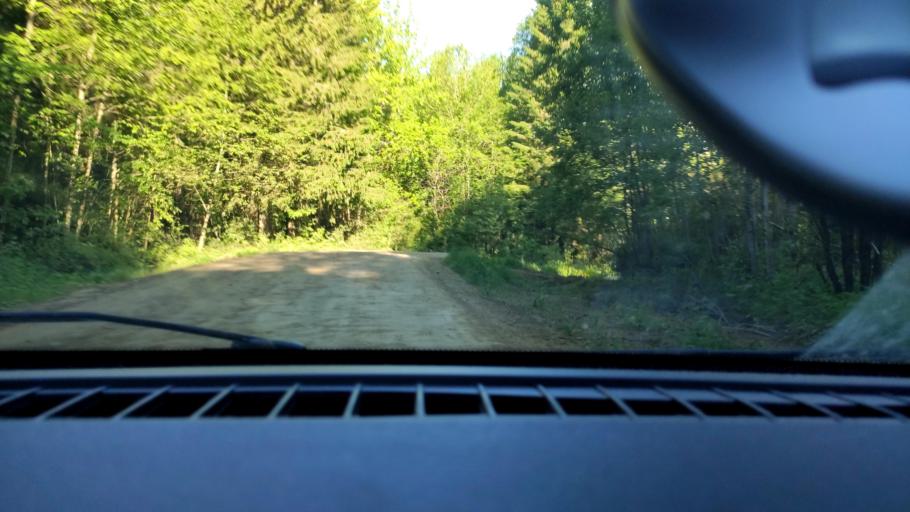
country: RU
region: Perm
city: Novyye Lyady
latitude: 58.1768
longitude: 56.5687
